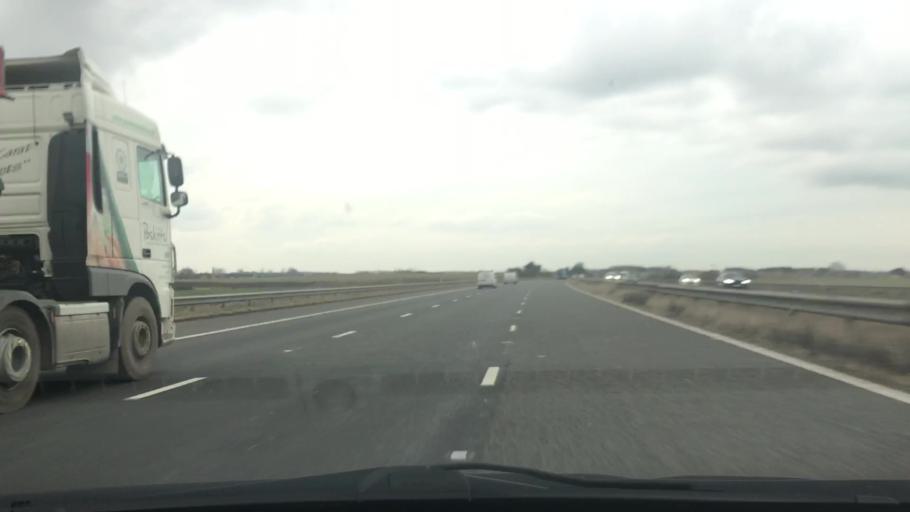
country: GB
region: England
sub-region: Doncaster
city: Hatfield
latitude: 53.5822
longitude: -0.9484
